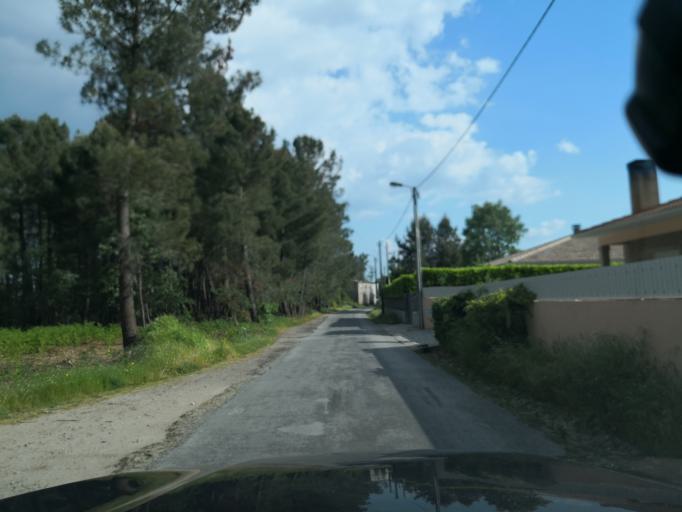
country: PT
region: Vila Real
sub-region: Vila Real
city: Vila Real
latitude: 41.3503
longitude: -7.7235
